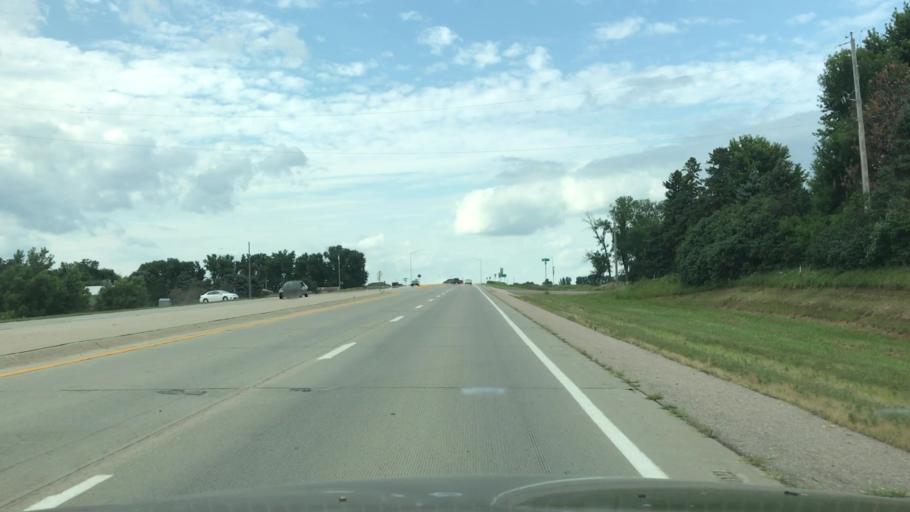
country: US
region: Iowa
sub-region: Plymouth County
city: Le Mars
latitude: 42.8130
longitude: -96.1747
